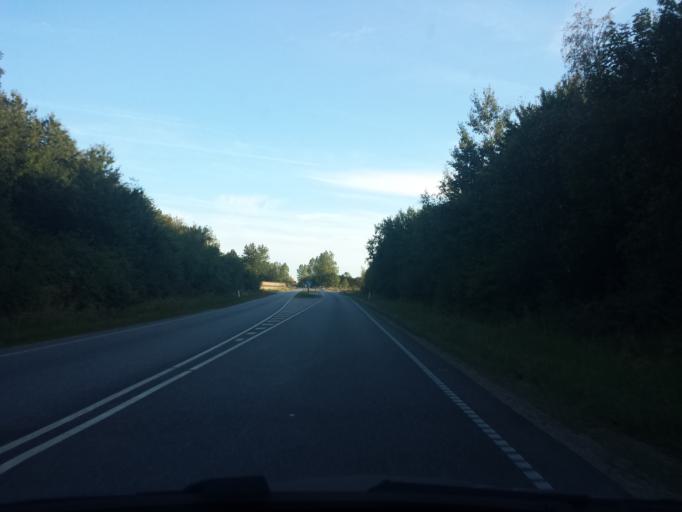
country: DK
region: Capital Region
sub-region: Frederikssund Kommune
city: Frederikssund
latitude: 55.8057
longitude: 12.1021
